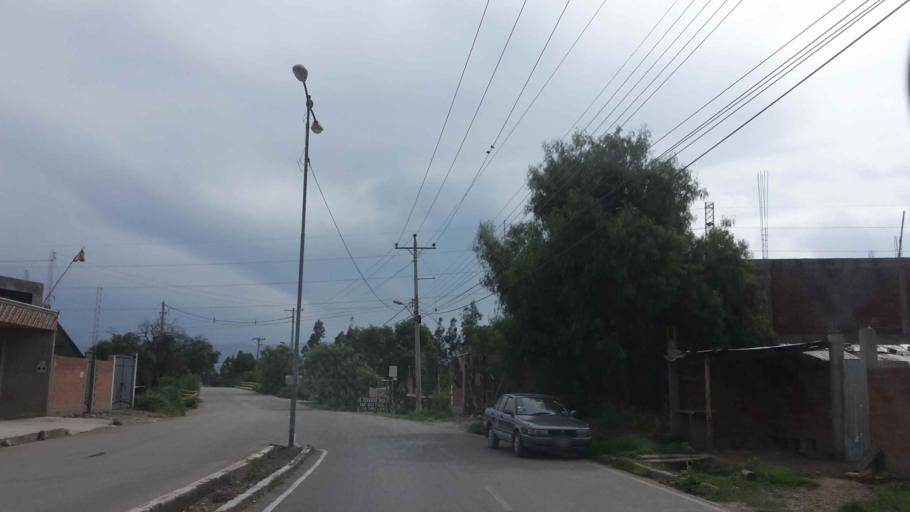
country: BO
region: Cochabamba
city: Cochabamba
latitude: -17.3333
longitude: -66.2533
